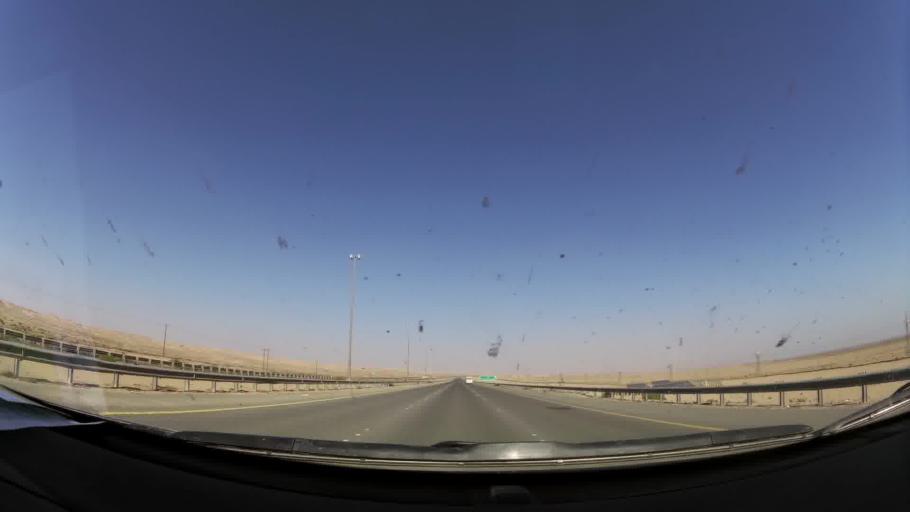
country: KW
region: Muhafazat al Jahra'
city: Al Jahra'
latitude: 29.5014
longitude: 47.7951
